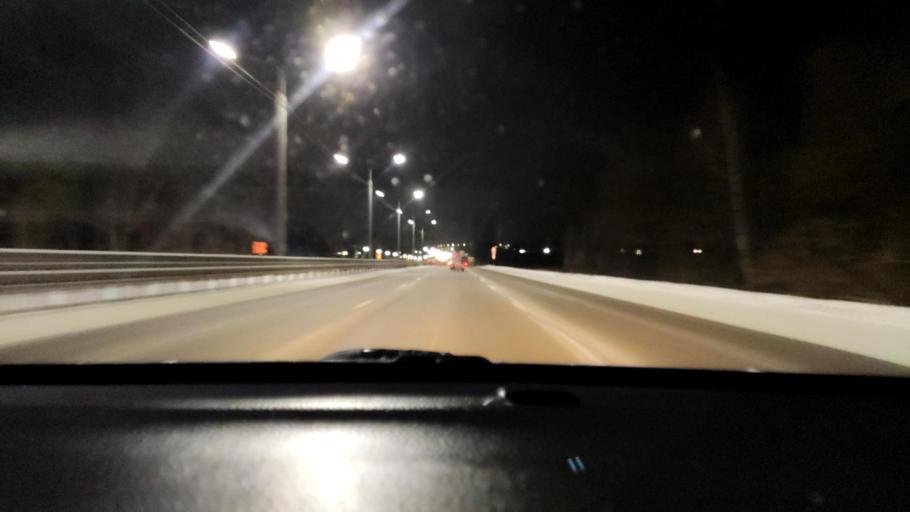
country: RU
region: Voronezj
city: Podgornoye
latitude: 51.8203
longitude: 39.2101
